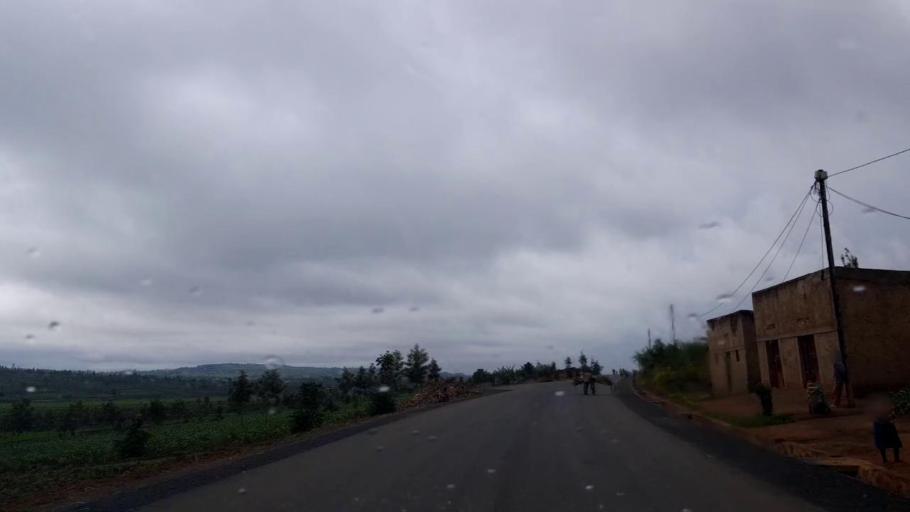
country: RW
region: Northern Province
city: Byumba
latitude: -1.4243
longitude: 30.2767
